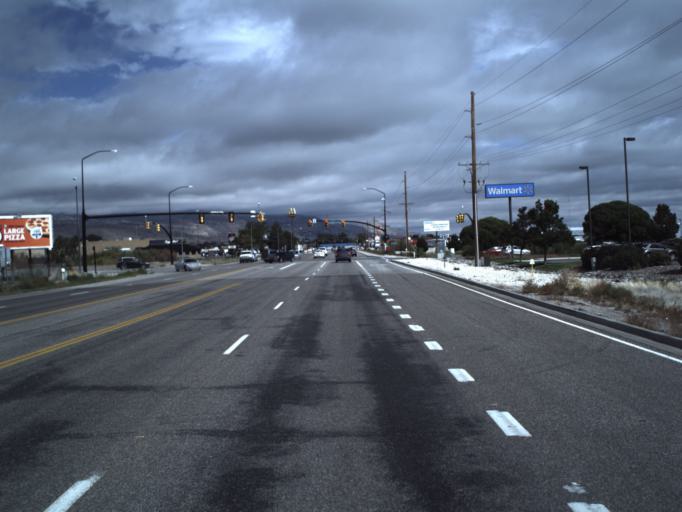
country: US
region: Utah
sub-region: Sevier County
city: Richfield
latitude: 38.7485
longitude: -112.0884
